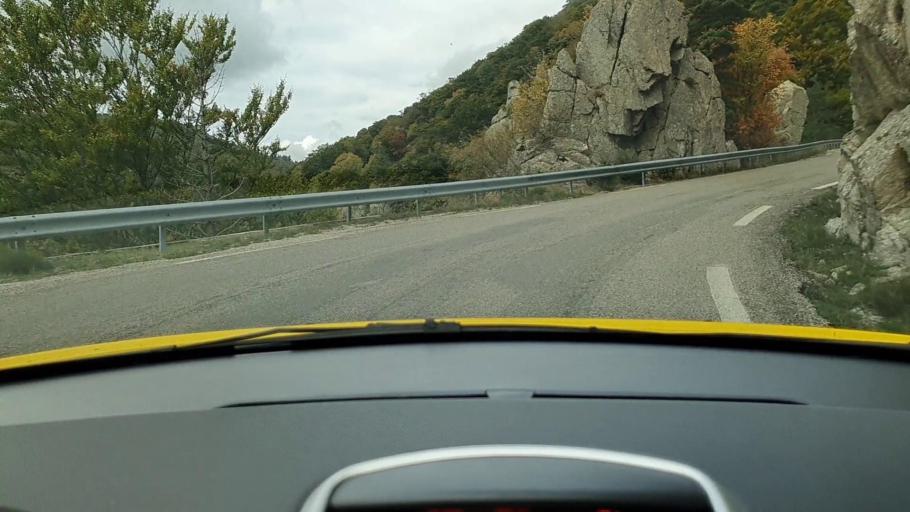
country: FR
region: Languedoc-Roussillon
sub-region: Departement du Gard
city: Le Vigan
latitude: 44.0427
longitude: 3.5590
